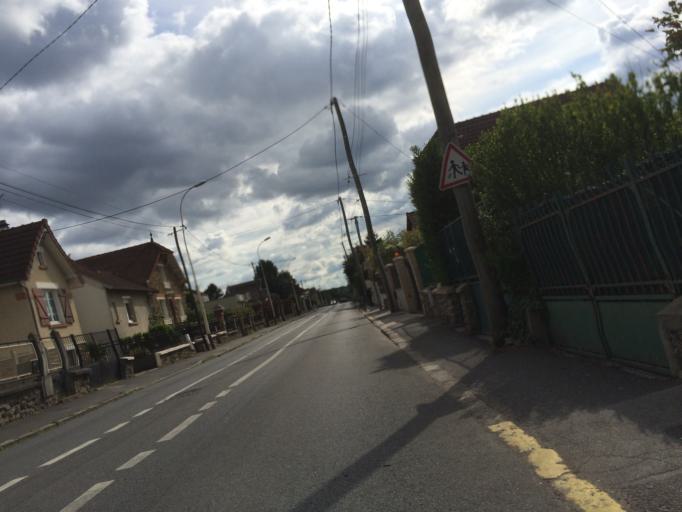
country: FR
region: Ile-de-France
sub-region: Departement de l'Essonne
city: Villiers-sur-Orge
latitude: 48.6504
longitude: 2.3065
